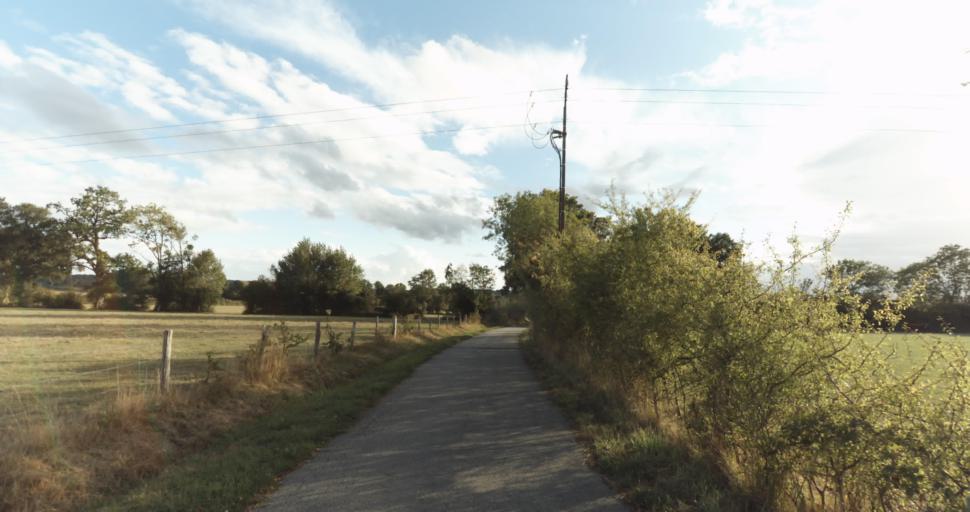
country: FR
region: Lower Normandy
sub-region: Departement de l'Orne
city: Sainte-Gauburge-Sainte-Colombe
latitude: 48.7275
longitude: 0.4090
